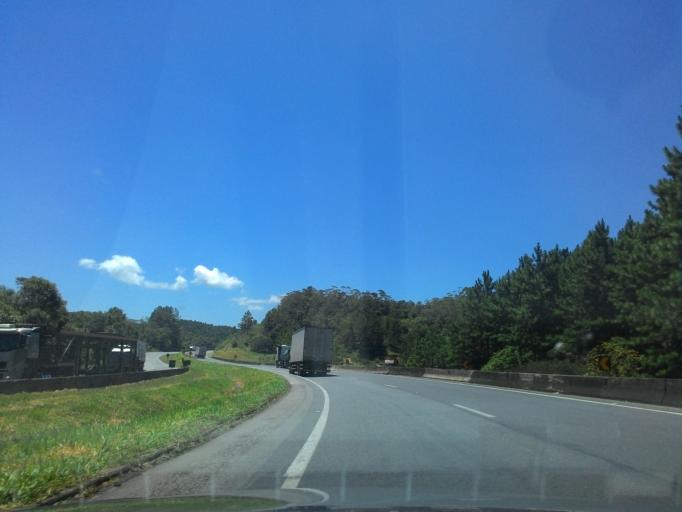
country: BR
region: Parana
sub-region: Antonina
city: Antonina
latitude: -25.1034
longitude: -48.7014
